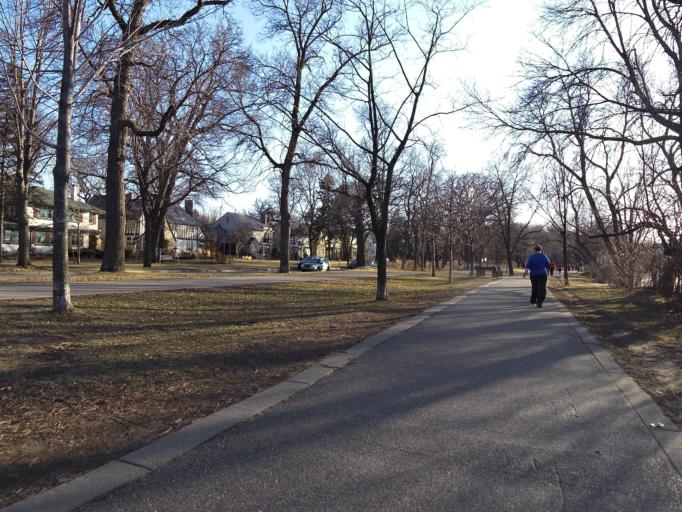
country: US
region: Minnesota
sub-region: Hennepin County
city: Richfield
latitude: 44.9168
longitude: -93.3008
